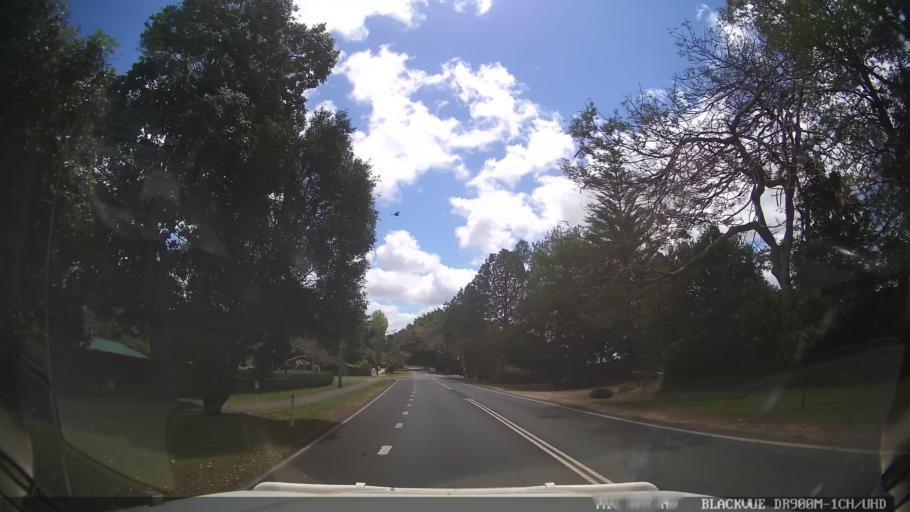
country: AU
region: Queensland
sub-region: Sunshine Coast
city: Nambour
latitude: -26.6624
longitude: 152.8830
